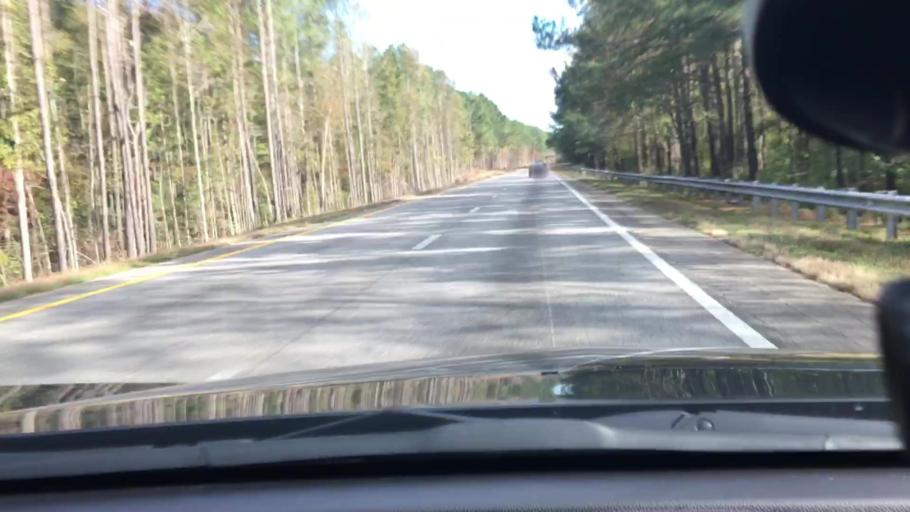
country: US
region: North Carolina
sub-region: Wake County
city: Zebulon
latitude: 35.7939
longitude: -78.1618
